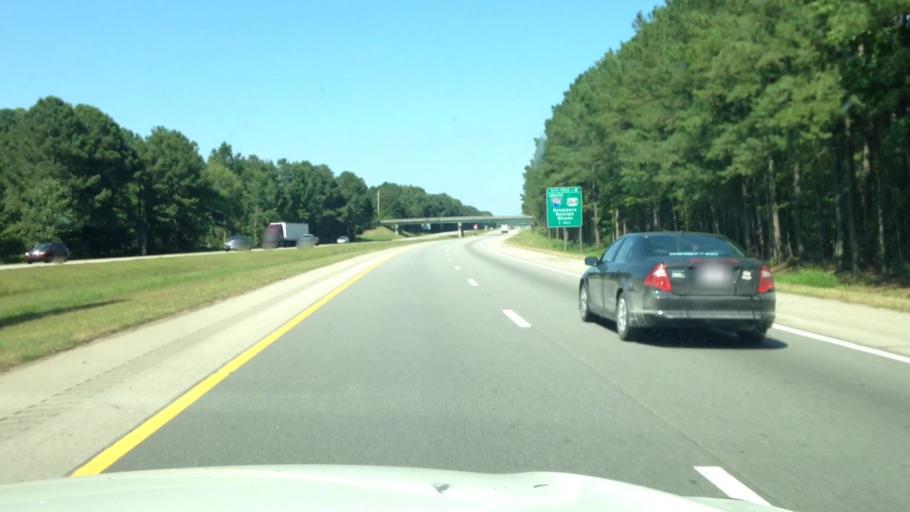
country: US
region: North Carolina
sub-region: Wilson County
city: Lucama
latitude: 35.7182
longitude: -78.0343
